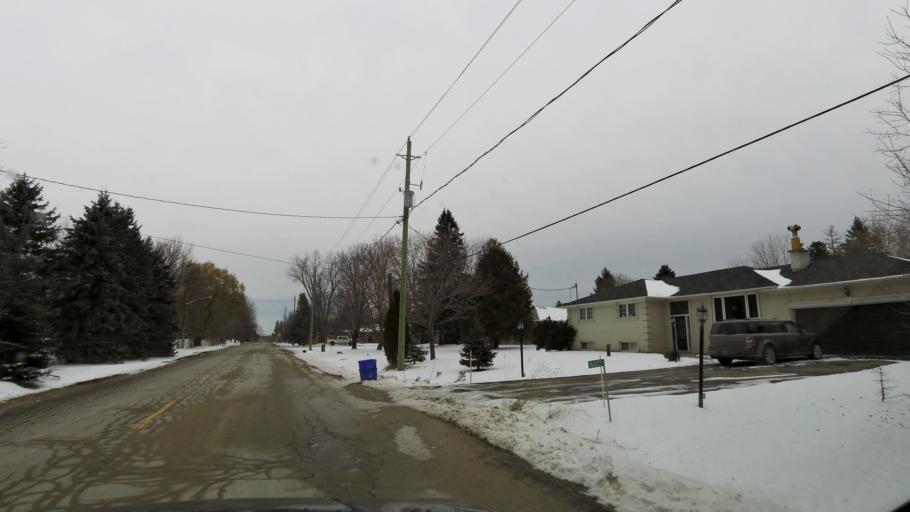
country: CA
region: Ontario
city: Bradford West Gwillimbury
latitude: 43.9855
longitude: -79.6215
